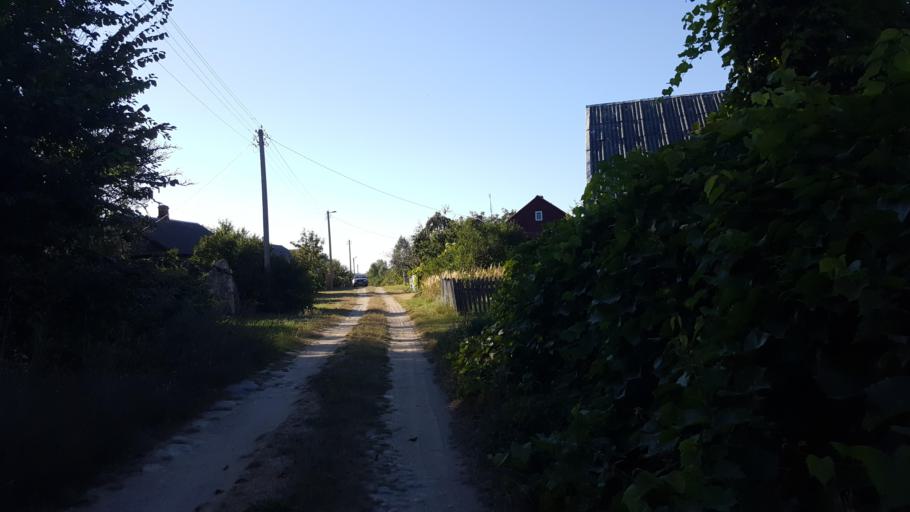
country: BY
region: Brest
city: Vysokaye
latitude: 52.3263
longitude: 23.2509
